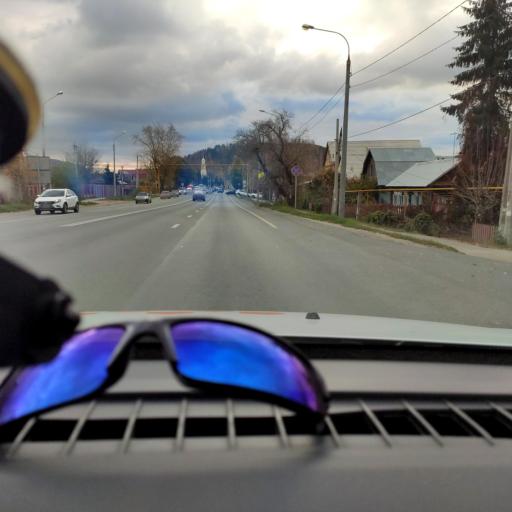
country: RU
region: Samara
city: Volzhskiy
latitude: 53.4297
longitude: 50.1190
